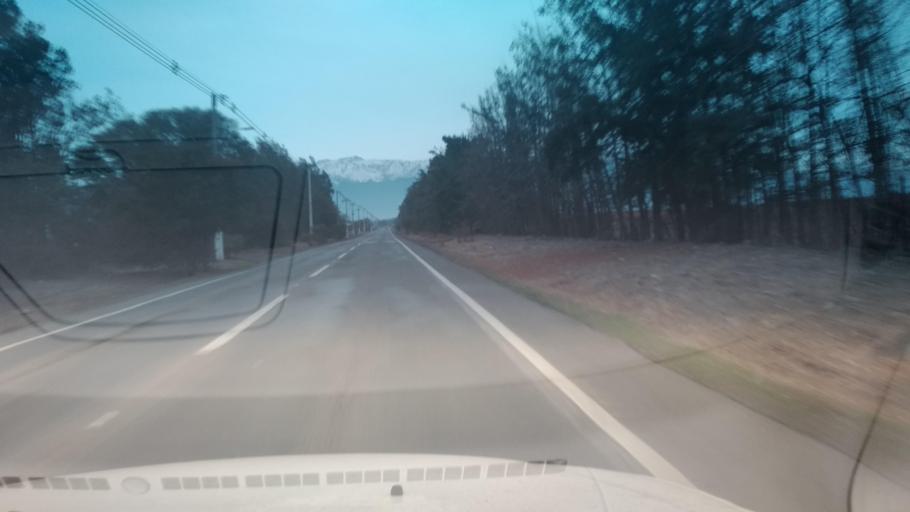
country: CL
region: Santiago Metropolitan
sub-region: Provincia de Chacabuco
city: Chicureo Abajo
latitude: -33.0944
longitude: -70.7016
